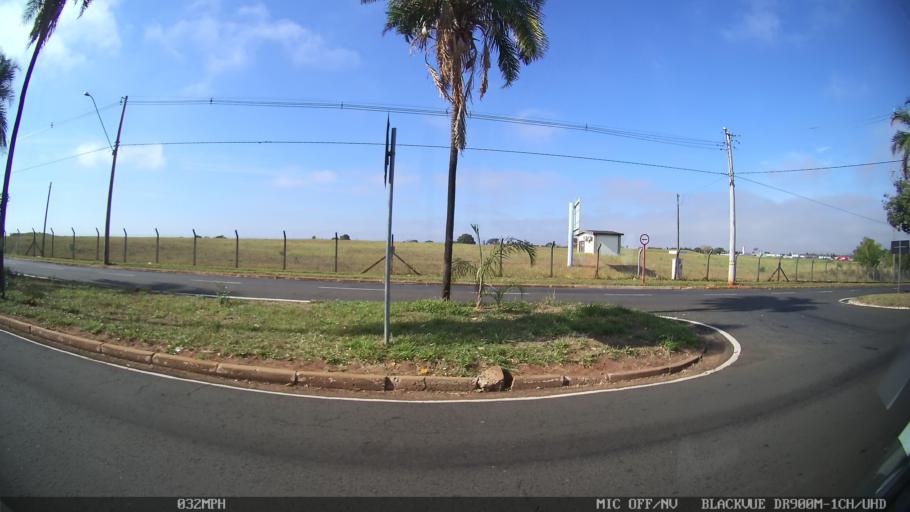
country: BR
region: Sao Paulo
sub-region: Sao Jose Do Rio Preto
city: Sao Jose do Rio Preto
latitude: -20.8198
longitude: -49.4150
